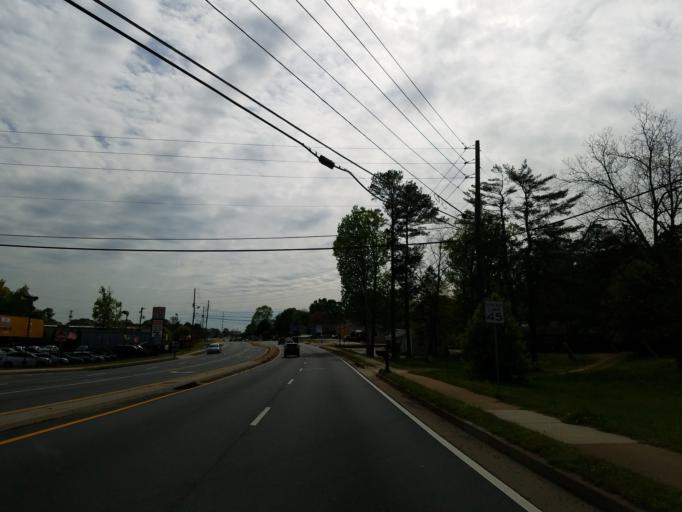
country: US
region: Georgia
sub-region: Cobb County
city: Fair Oaks
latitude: 33.9027
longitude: -84.5681
